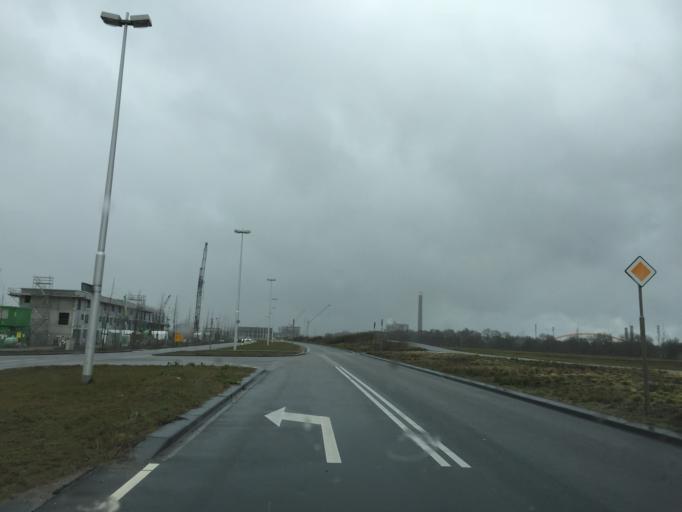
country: NL
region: Utrecht
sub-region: Gemeente Utrecht
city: Utrecht
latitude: 52.0886
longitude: 5.0743
